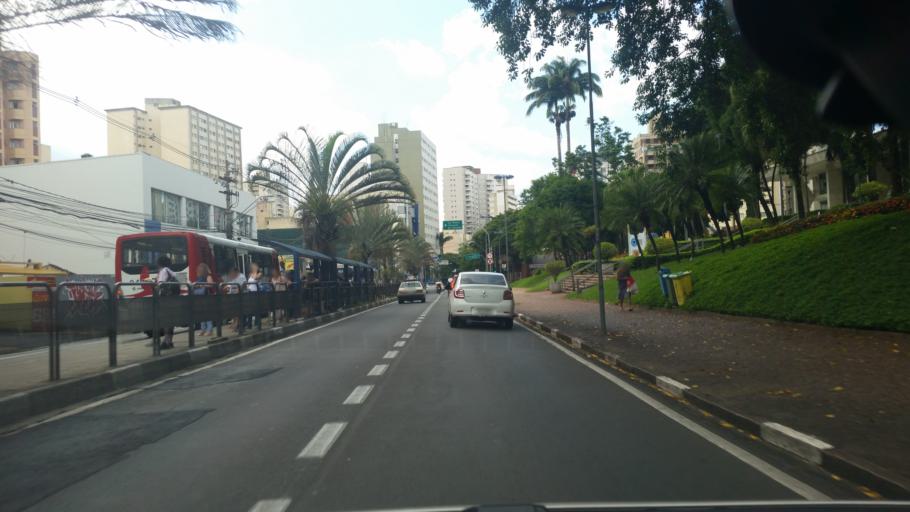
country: BR
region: Sao Paulo
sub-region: Campinas
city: Campinas
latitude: -22.9016
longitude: -47.0577
